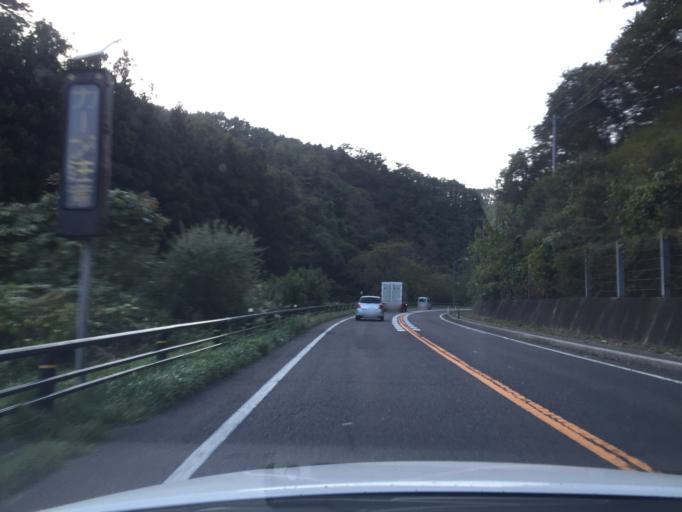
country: JP
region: Fukushima
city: Sukagawa
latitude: 37.2949
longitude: 140.5200
